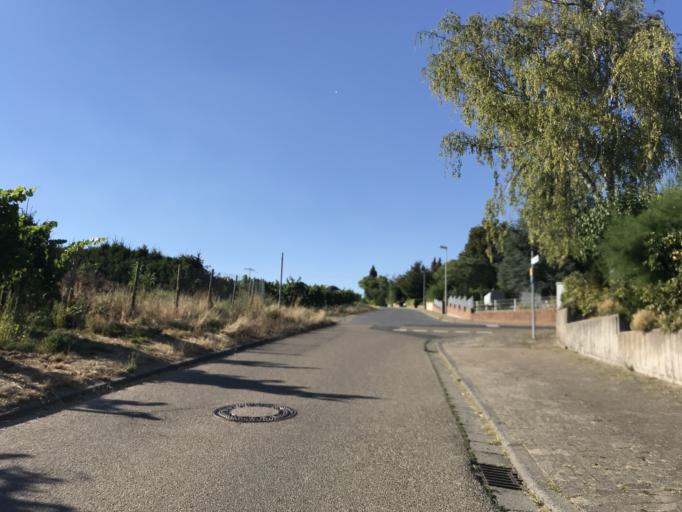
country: DE
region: Rheinland-Pfalz
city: Stadecken-Elsheim
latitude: 49.9197
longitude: 8.1227
